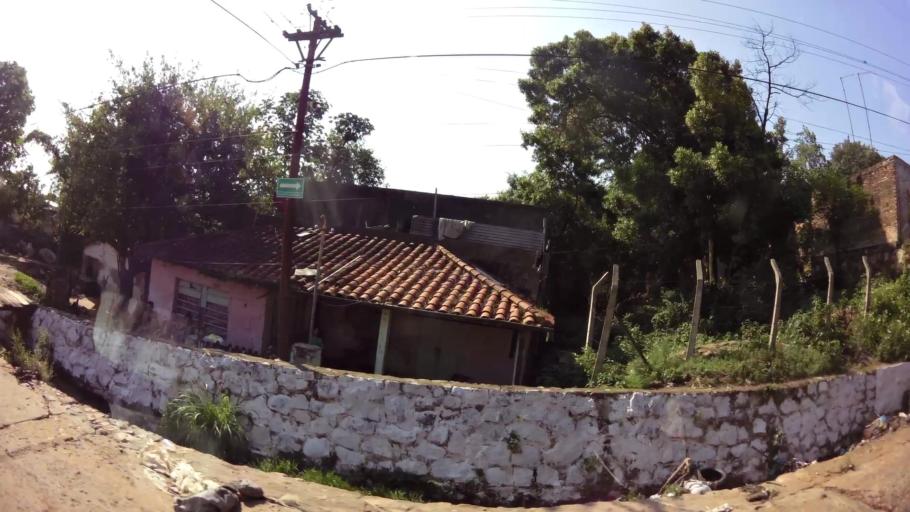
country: PY
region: Asuncion
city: Asuncion
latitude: -25.3240
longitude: -57.6409
